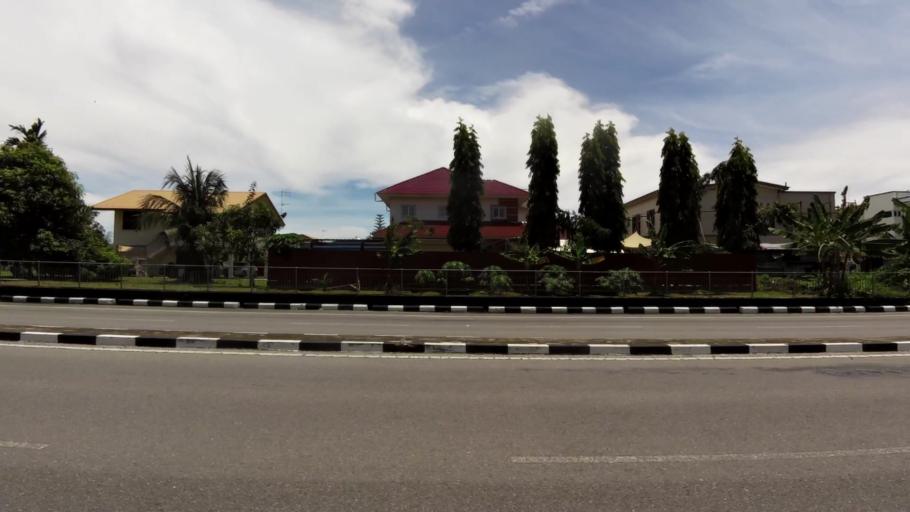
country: BN
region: Belait
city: Kuala Belait
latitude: 4.5867
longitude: 114.2468
